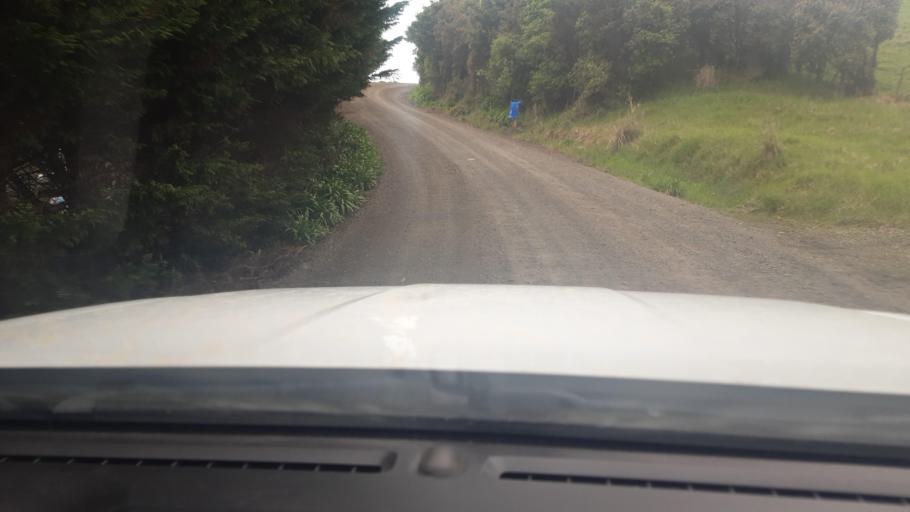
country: NZ
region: Northland
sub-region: Far North District
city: Kaitaia
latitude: -35.0734
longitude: 173.3249
